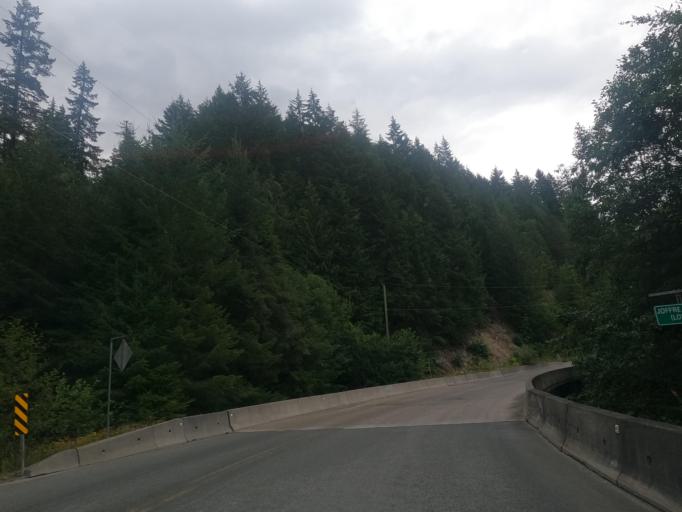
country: CA
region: British Columbia
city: Pemberton
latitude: 50.3034
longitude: -122.5899
